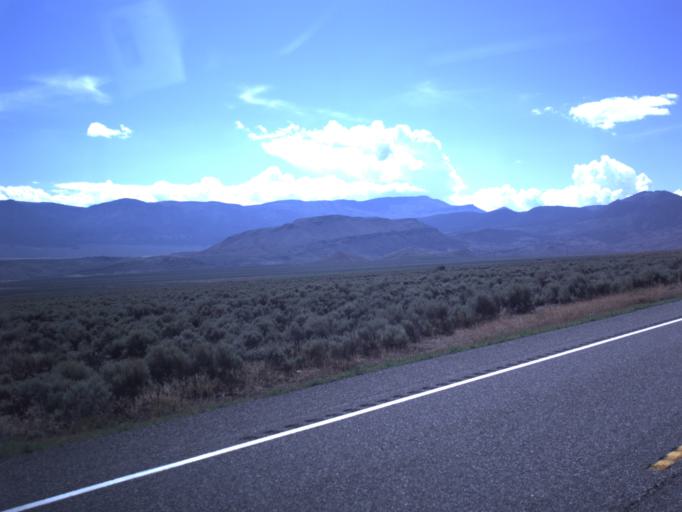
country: US
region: Utah
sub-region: Piute County
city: Junction
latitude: 38.3655
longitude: -112.2241
